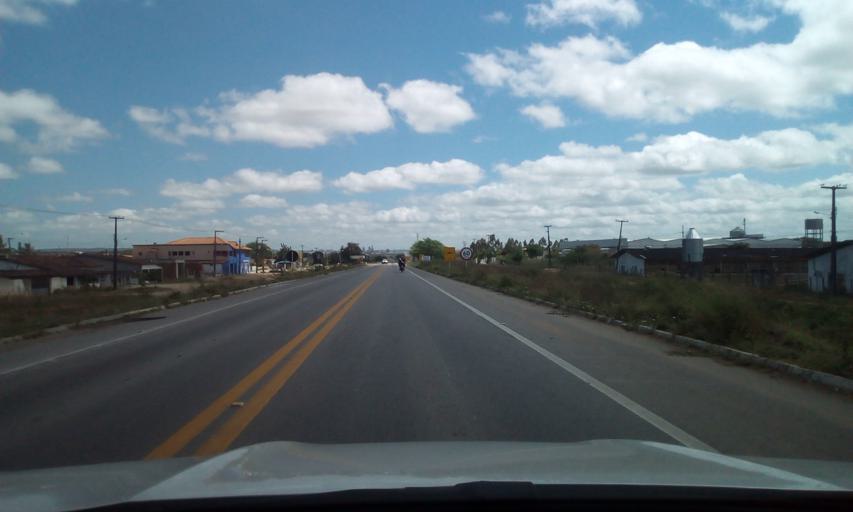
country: BR
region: Paraiba
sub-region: Campina Grande
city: Campina Grande
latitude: -7.3056
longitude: -35.8930
